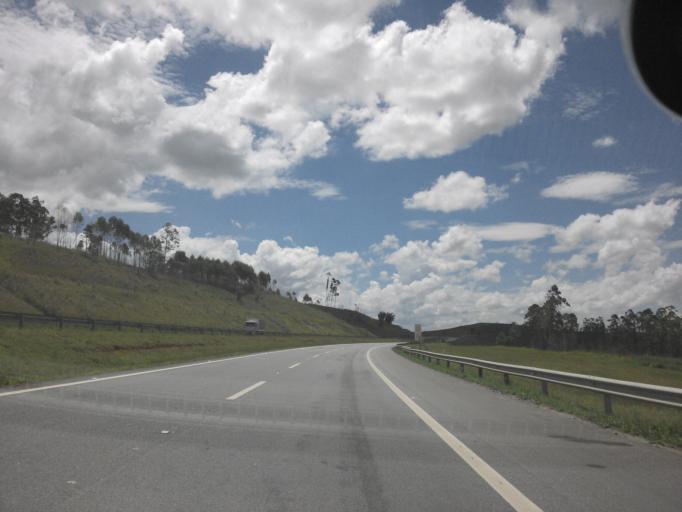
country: BR
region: Sao Paulo
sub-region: Jacarei
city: Jacarei
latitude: -23.3365
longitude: -46.0244
